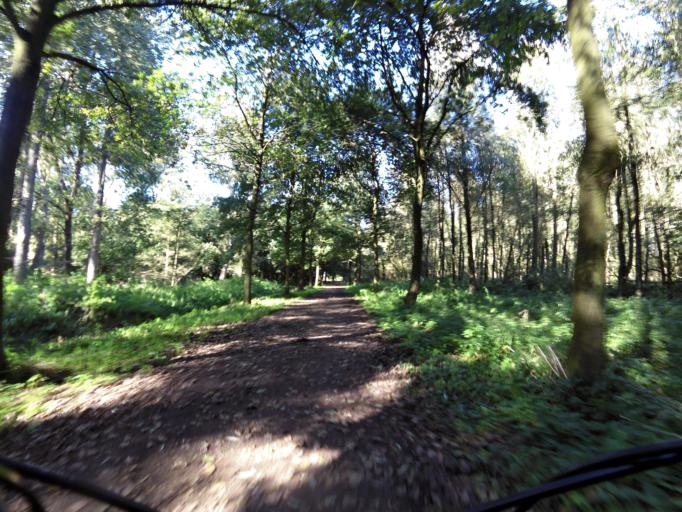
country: NL
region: South Holland
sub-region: Gemeente Voorschoten
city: Voorschoten
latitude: 52.0958
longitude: 4.4265
